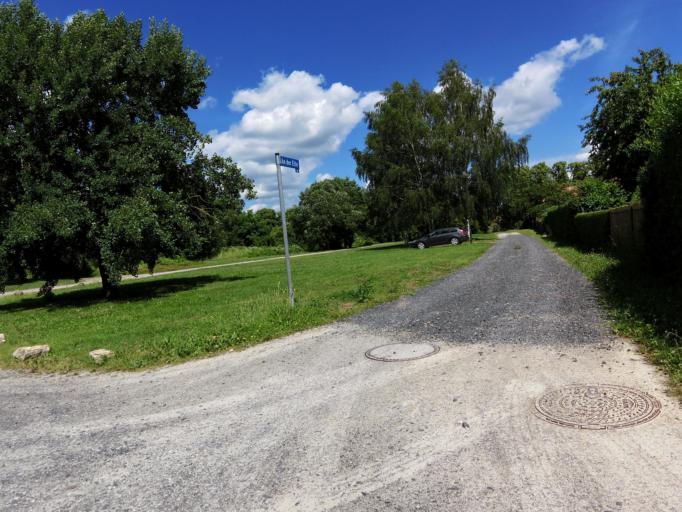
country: DE
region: Thuringia
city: Lauchroden
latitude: 50.9953
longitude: 10.1574
